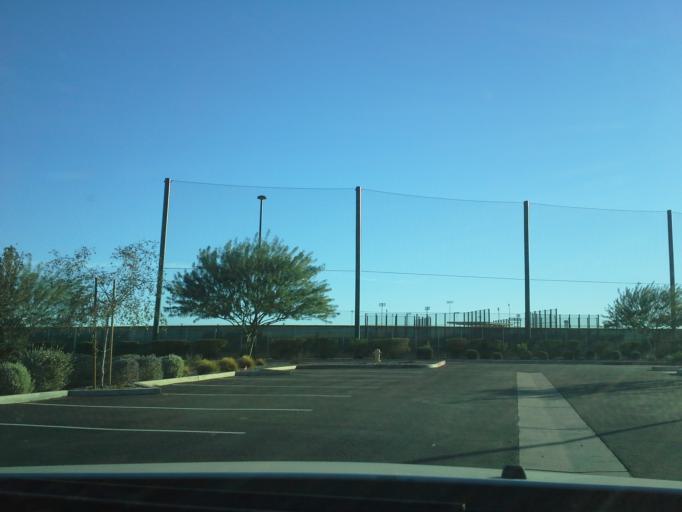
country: US
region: Arizona
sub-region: Maricopa County
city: Tempe
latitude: 33.4309
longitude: -111.8891
